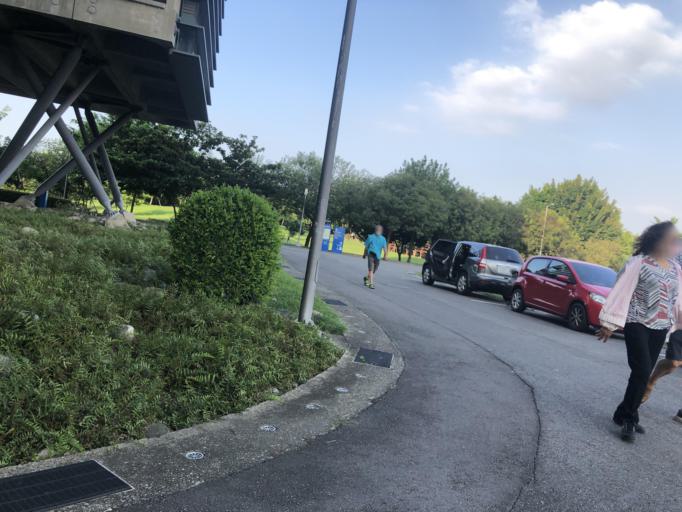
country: TW
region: Taiwan
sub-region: Tainan
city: Tainan
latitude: 23.0580
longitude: 120.2360
